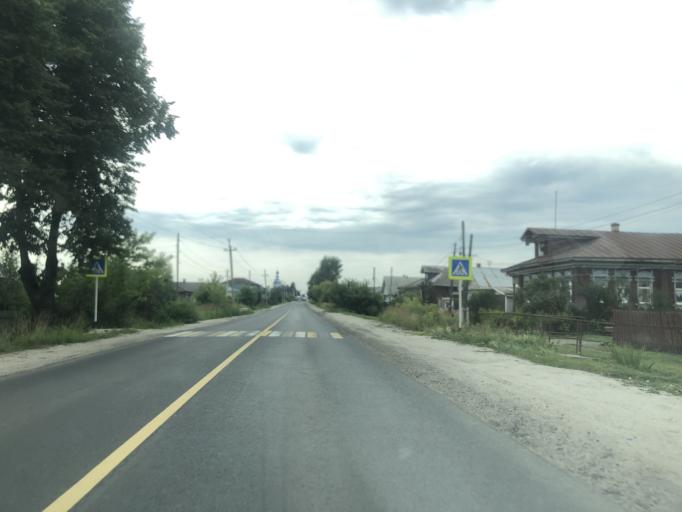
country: RU
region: Ivanovo
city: Pestyaki
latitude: 56.7055
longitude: 42.6779
